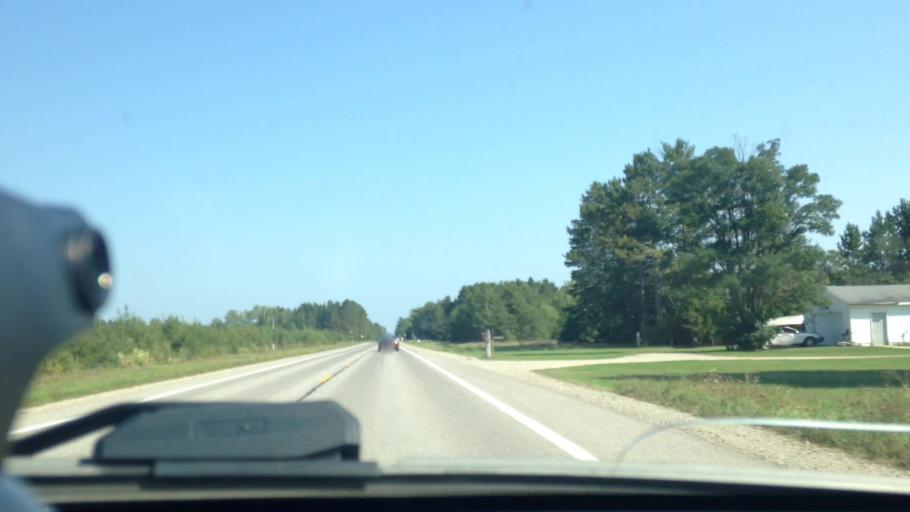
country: US
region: Michigan
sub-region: Luce County
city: Newberry
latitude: 46.3036
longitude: -85.4536
